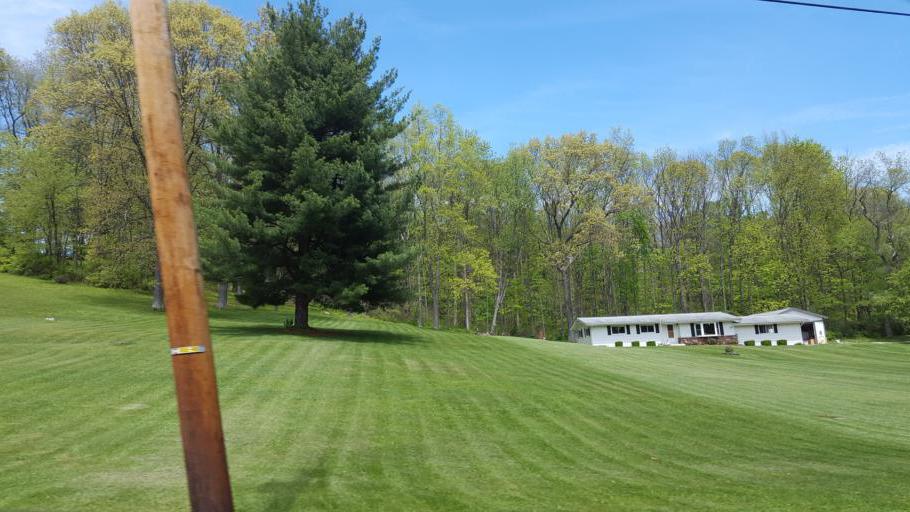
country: US
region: Ohio
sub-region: Knox County
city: Gambier
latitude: 40.3898
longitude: -82.4277
